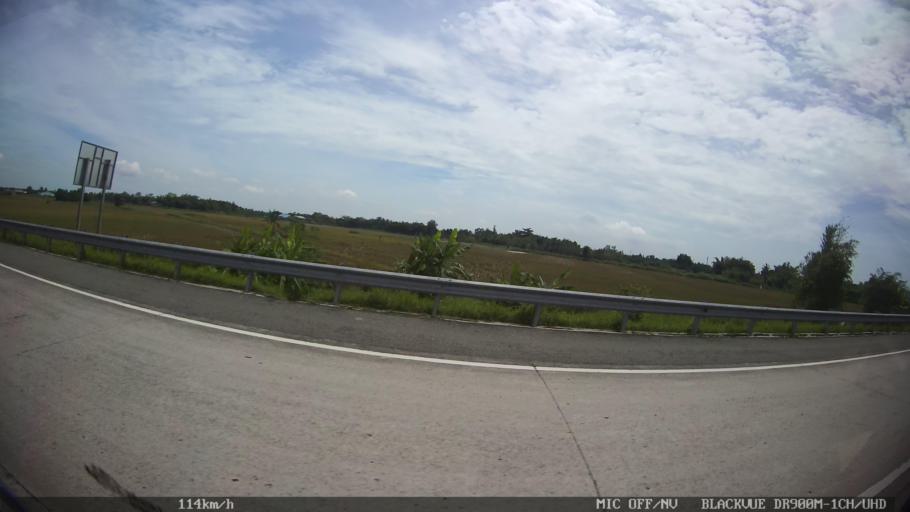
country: ID
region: North Sumatra
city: Percut
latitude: 3.5656
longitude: 98.8492
